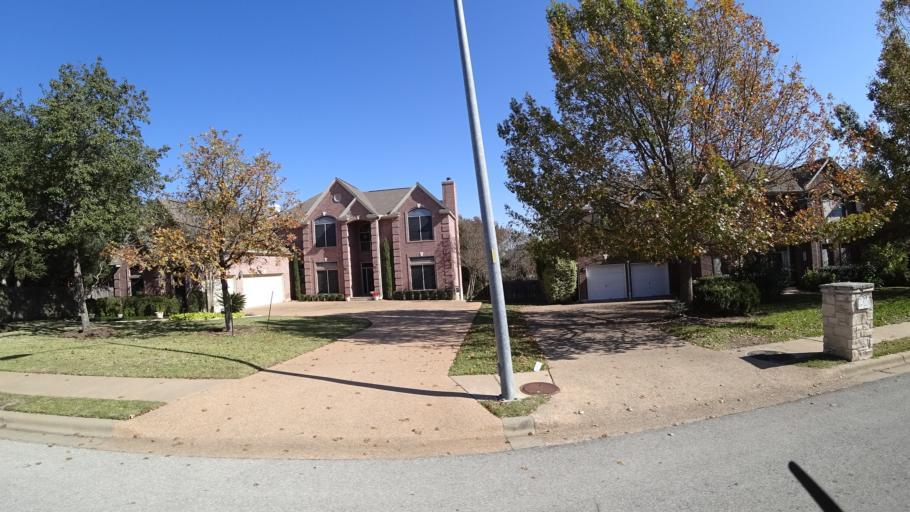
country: US
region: Texas
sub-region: Travis County
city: Lost Creek
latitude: 30.3783
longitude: -97.8526
